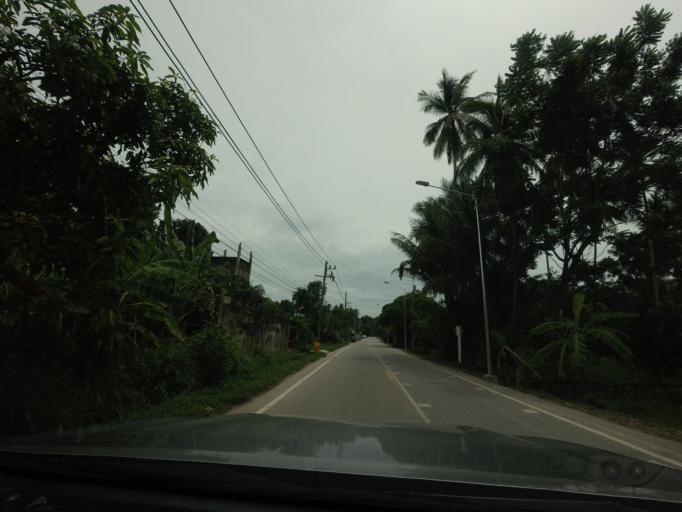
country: TH
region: Pattani
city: Kapho
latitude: 6.5853
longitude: 101.5344
